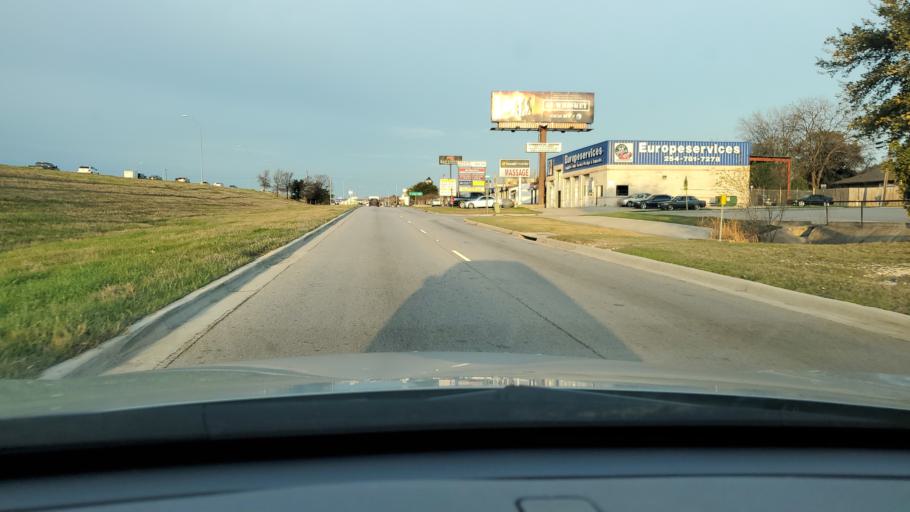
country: US
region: Texas
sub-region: Bell County
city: Killeen
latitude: 31.0943
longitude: -97.7289
